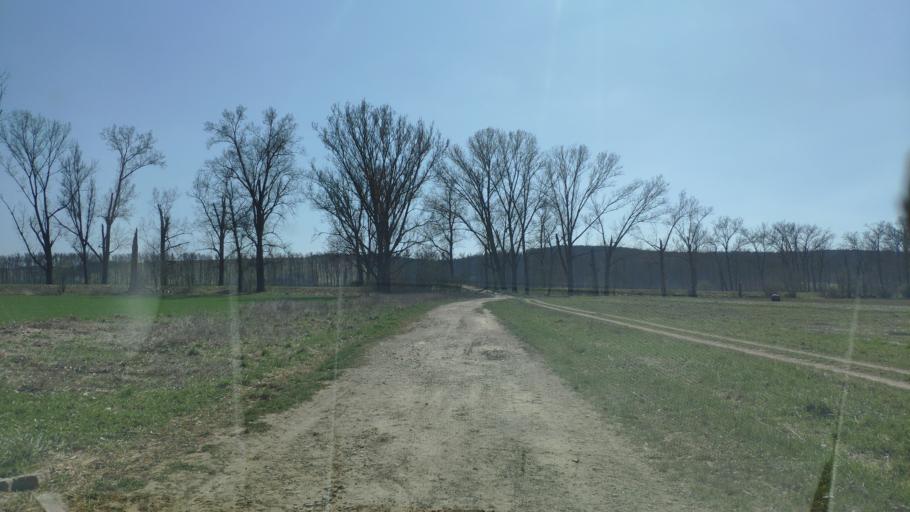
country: SK
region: Kosicky
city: Moldava nad Bodvou
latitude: 48.5736
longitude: 20.9470
